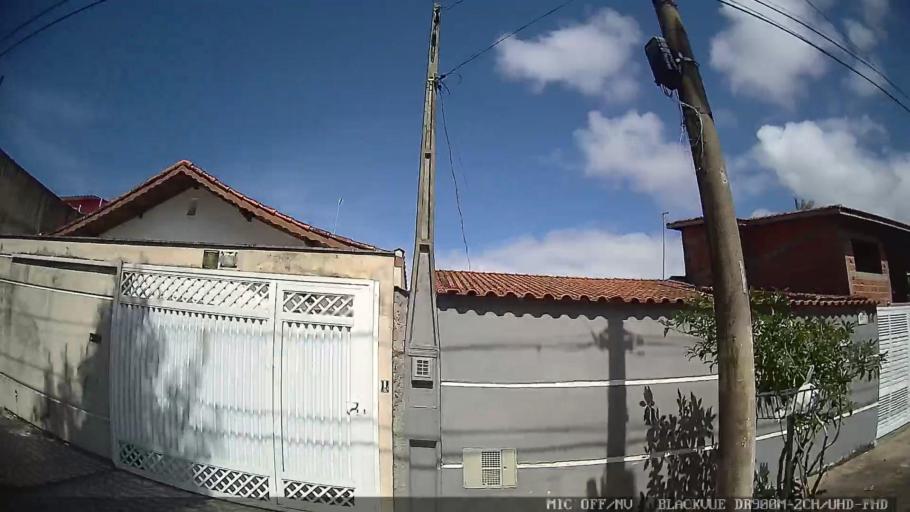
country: BR
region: Sao Paulo
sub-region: Peruibe
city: Peruibe
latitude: -24.3082
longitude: -47.0055
